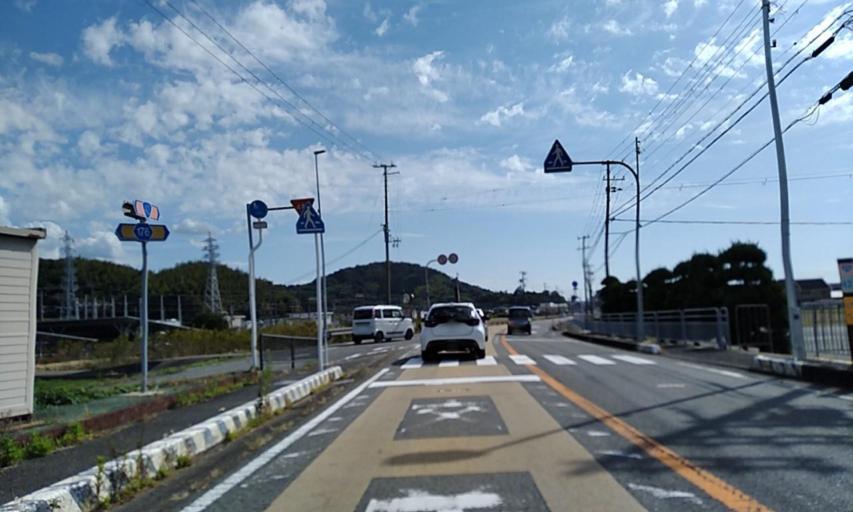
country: JP
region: Wakayama
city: Gobo
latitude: 33.9218
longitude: 135.1455
